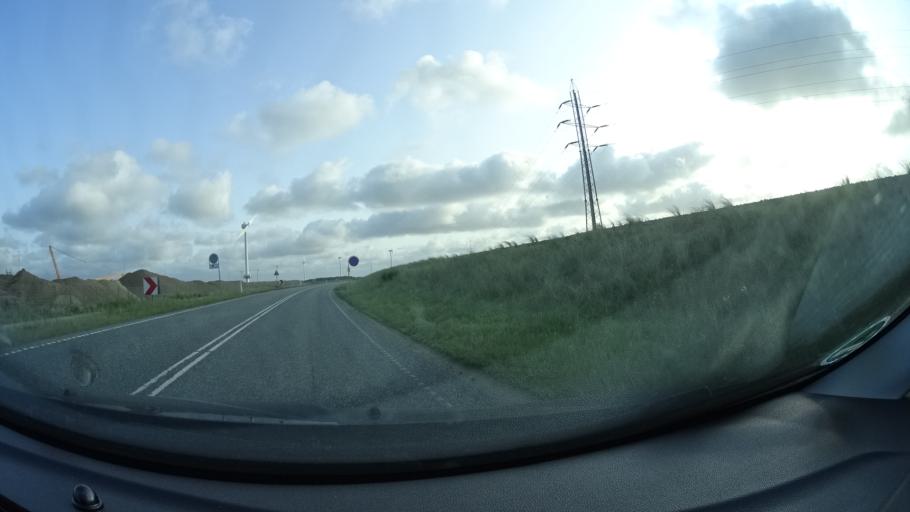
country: DK
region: Central Jutland
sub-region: Lemvig Kommune
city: Thyboron
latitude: 56.6809
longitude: 8.2239
